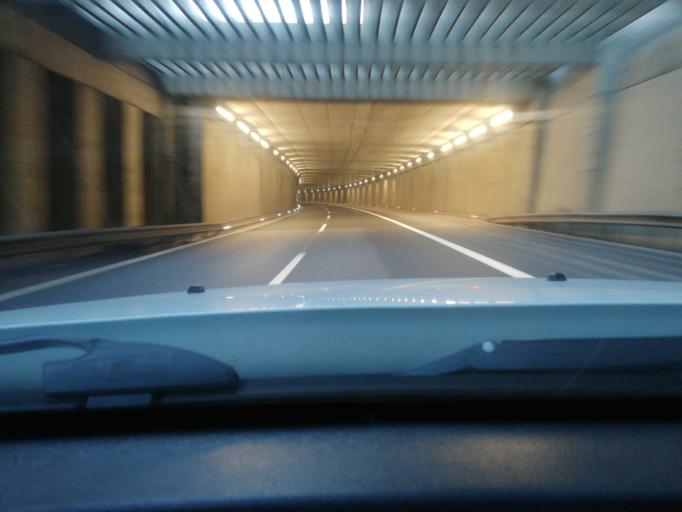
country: TR
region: Kocaeli
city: Derince
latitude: 40.7620
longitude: 29.8591
